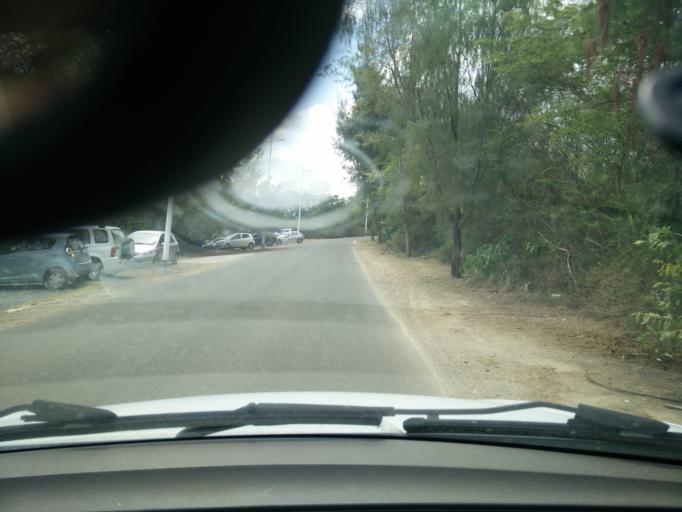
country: GP
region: Guadeloupe
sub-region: Guadeloupe
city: Pointe-a-Pitre
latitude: 16.2243
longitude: -61.5508
